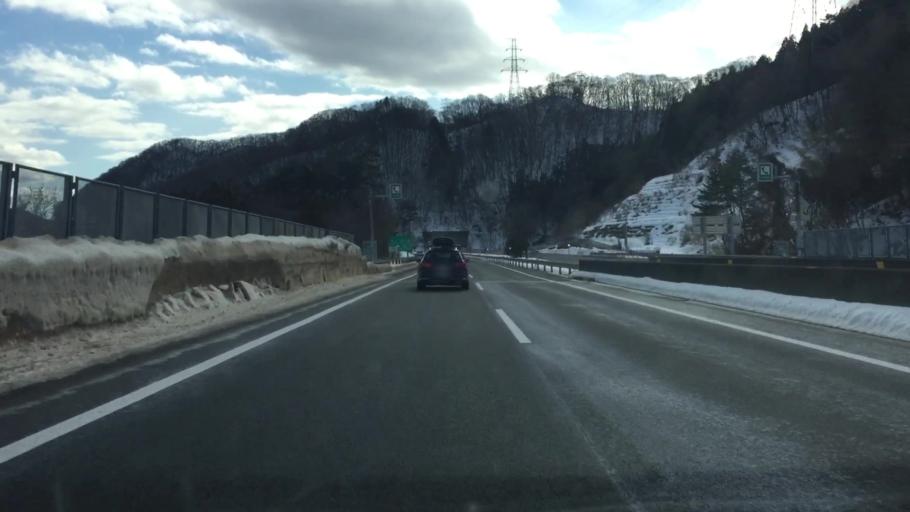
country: JP
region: Gunma
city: Numata
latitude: 36.7593
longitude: 138.9663
